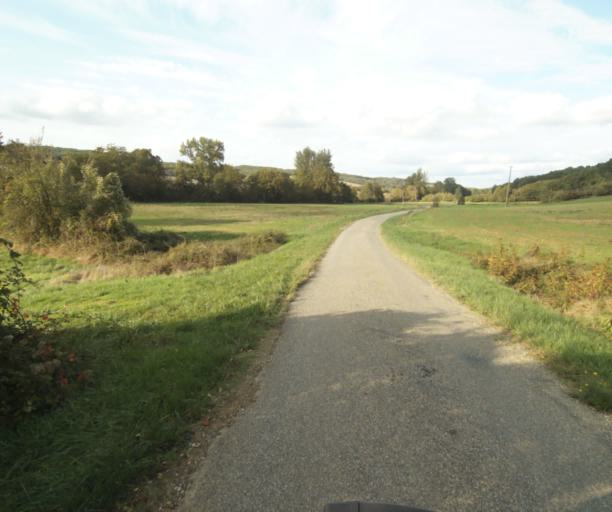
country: FR
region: Midi-Pyrenees
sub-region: Departement de la Haute-Garonne
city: Launac
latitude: 43.8197
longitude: 1.0896
